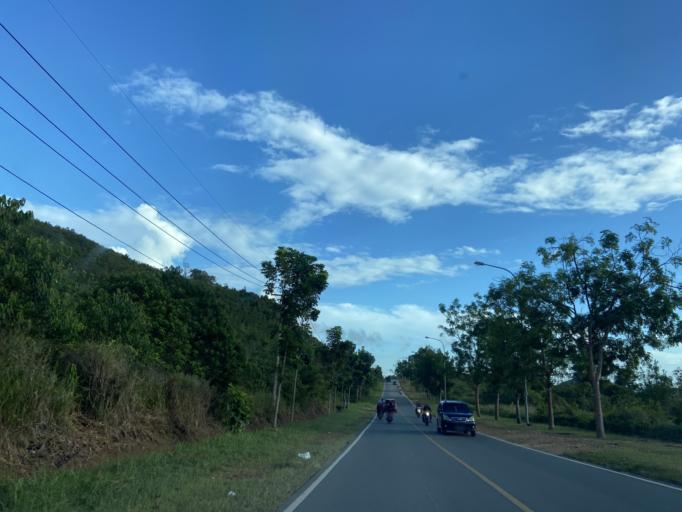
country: SG
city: Singapore
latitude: 0.9878
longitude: 104.0371
